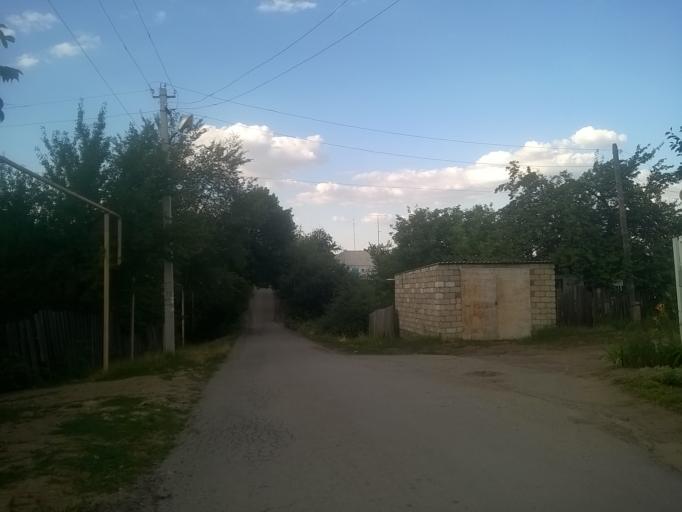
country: RU
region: Rostov
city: Donetsk
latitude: 48.3406
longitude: 39.9599
